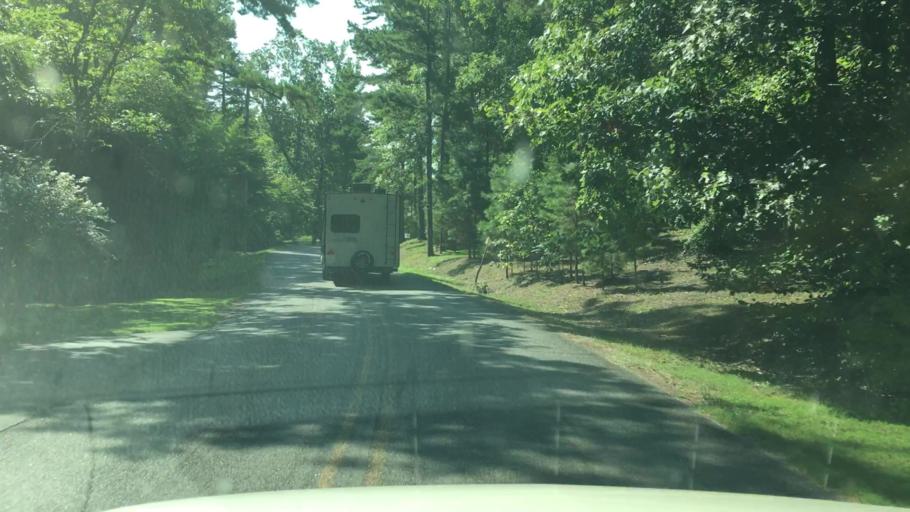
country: US
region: Arkansas
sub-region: Garland County
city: Piney
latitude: 34.5310
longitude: -93.3375
